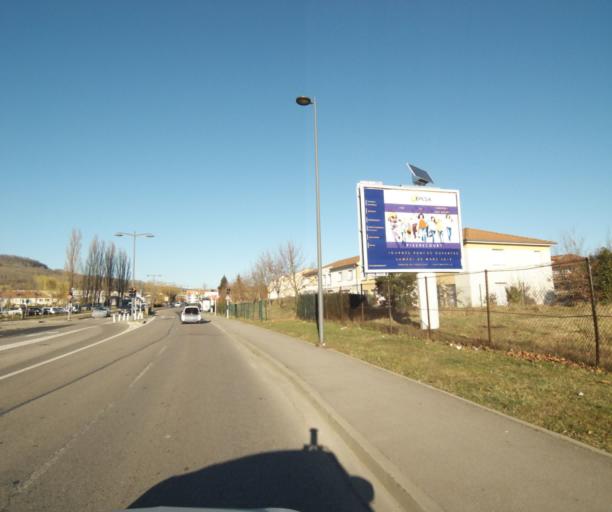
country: FR
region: Lorraine
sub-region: Departement de Meurthe-et-Moselle
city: Essey-les-Nancy
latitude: 48.7011
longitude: 6.2252
